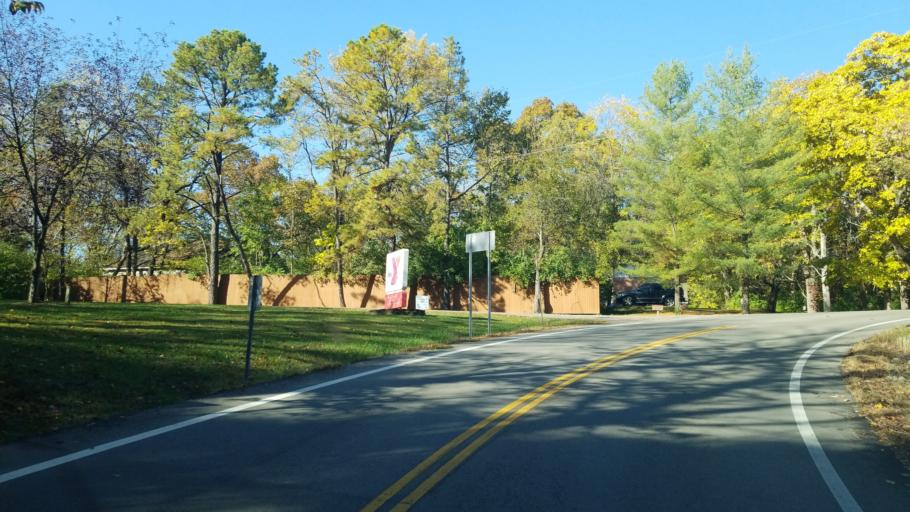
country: US
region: Ohio
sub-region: Warren County
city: Morrow
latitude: 39.4053
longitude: -84.1068
